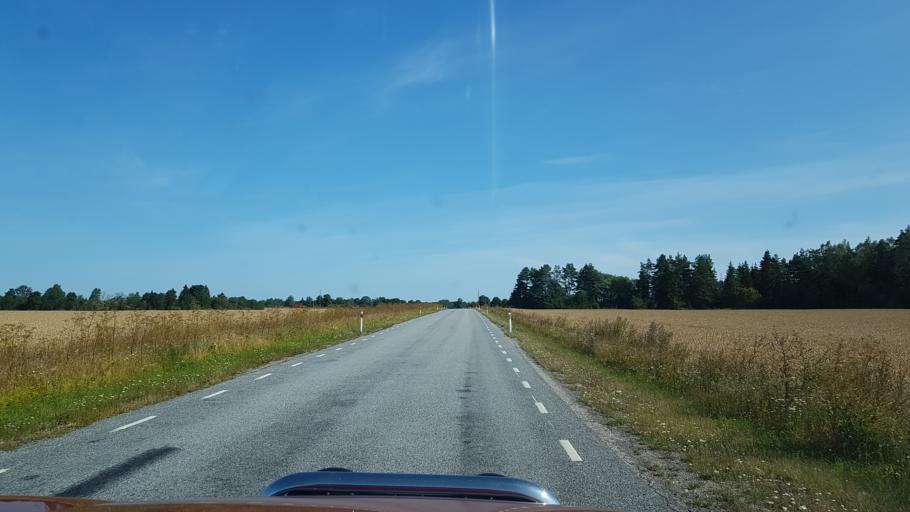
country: EE
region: Harju
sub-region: Raasiku vald
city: Raasiku
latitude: 59.2912
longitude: 25.1689
